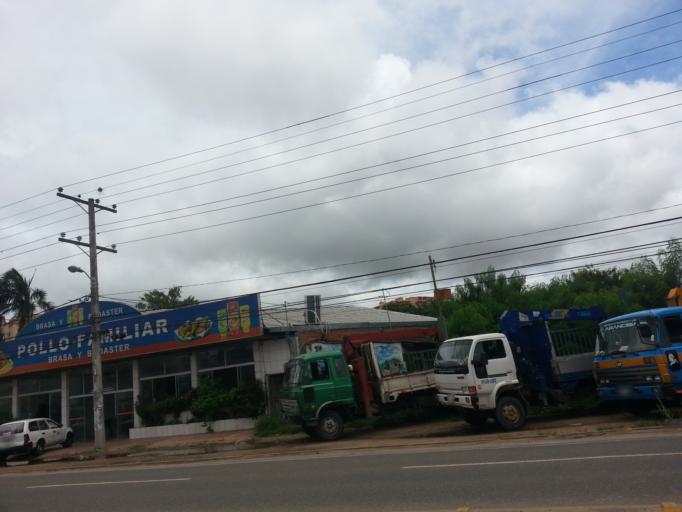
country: BO
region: Santa Cruz
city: Santa Cruz de la Sierra
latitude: -17.7421
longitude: -63.1722
